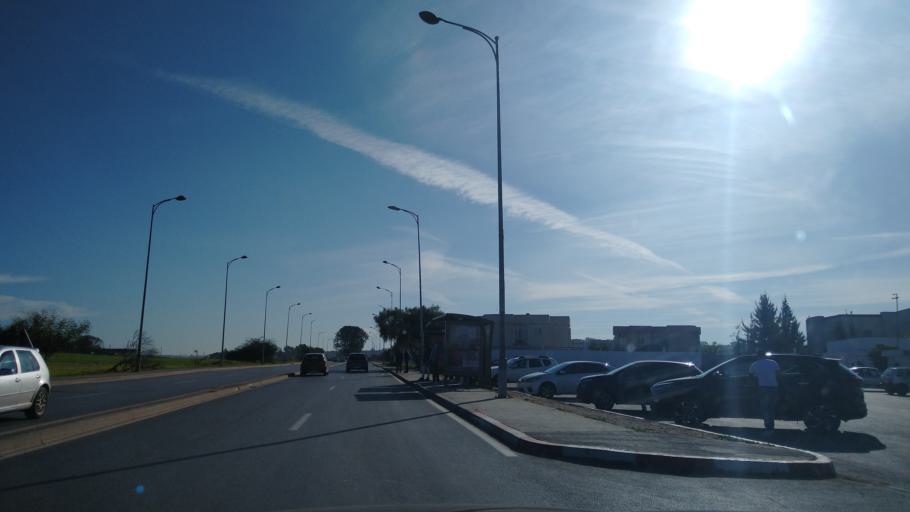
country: MA
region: Rabat-Sale-Zemmour-Zaer
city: Sale
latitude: 34.0197
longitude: -6.7348
